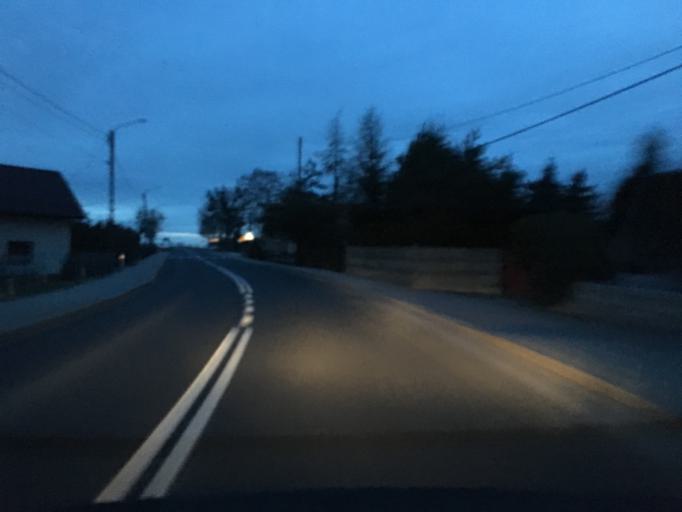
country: PL
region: Opole Voivodeship
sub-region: Powiat brzeski
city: Lewin Brzeski
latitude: 50.7740
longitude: 17.6226
